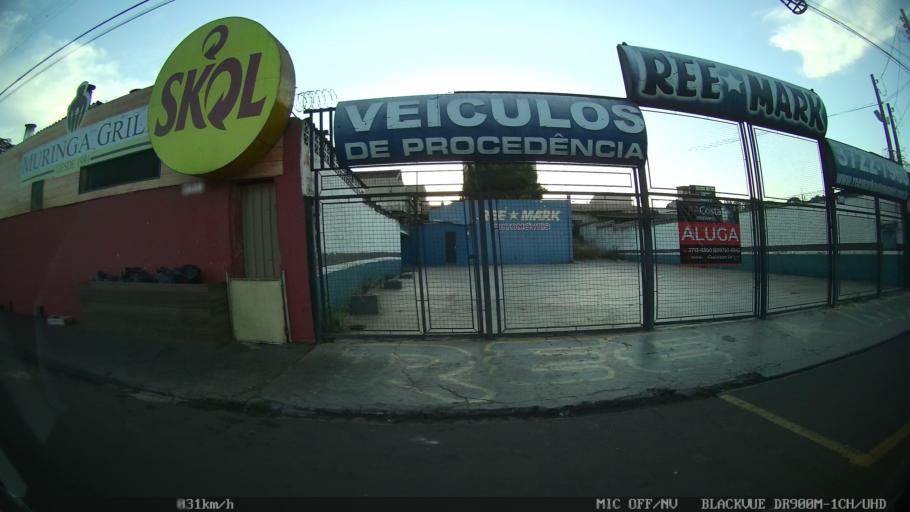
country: BR
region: Sao Paulo
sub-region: Franca
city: Franca
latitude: -20.5304
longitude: -47.4040
